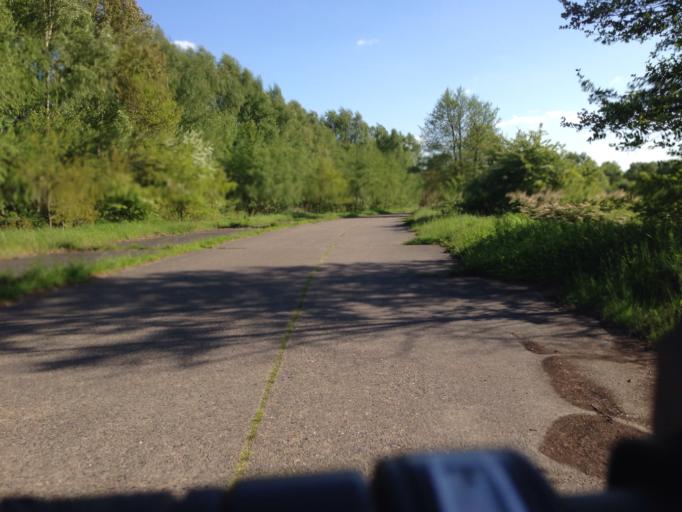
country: DE
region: Schleswig-Holstein
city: Stapelfeld
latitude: 53.6236
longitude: 10.2078
